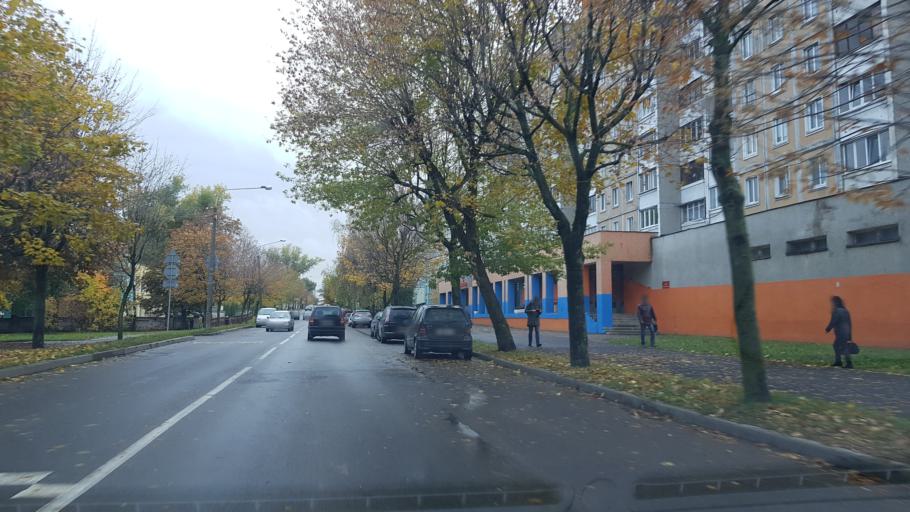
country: BY
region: Minsk
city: Syenitsa
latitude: 53.8491
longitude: 27.5515
